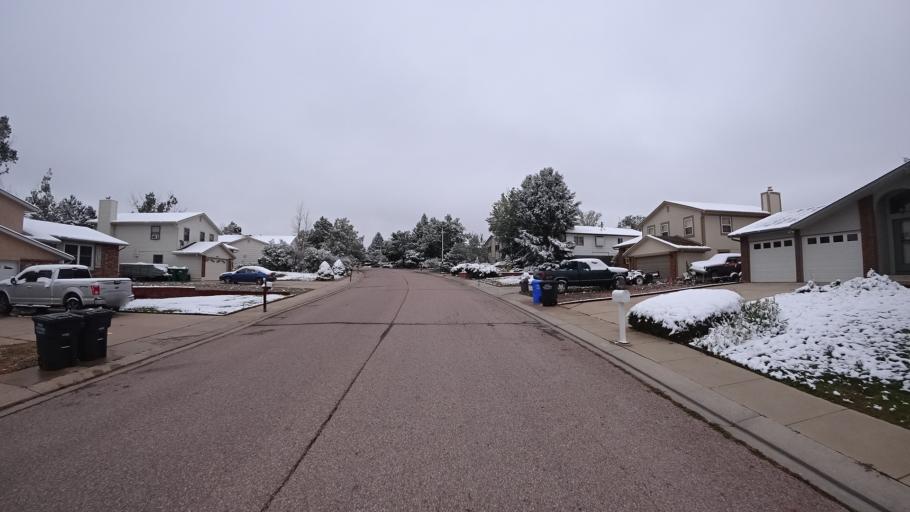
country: US
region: Colorado
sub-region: El Paso County
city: Colorado Springs
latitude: 38.9249
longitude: -104.7881
